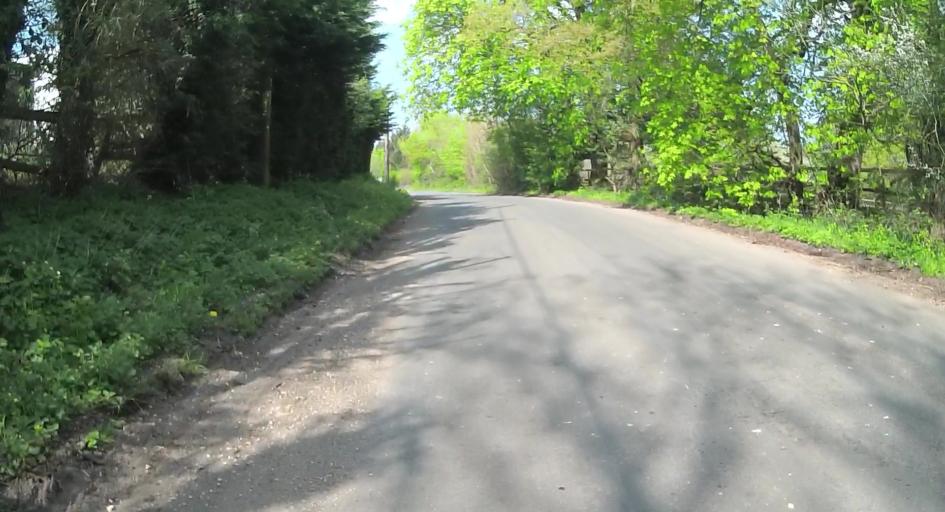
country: GB
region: England
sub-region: Hampshire
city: Tadley
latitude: 51.3768
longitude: -1.1268
